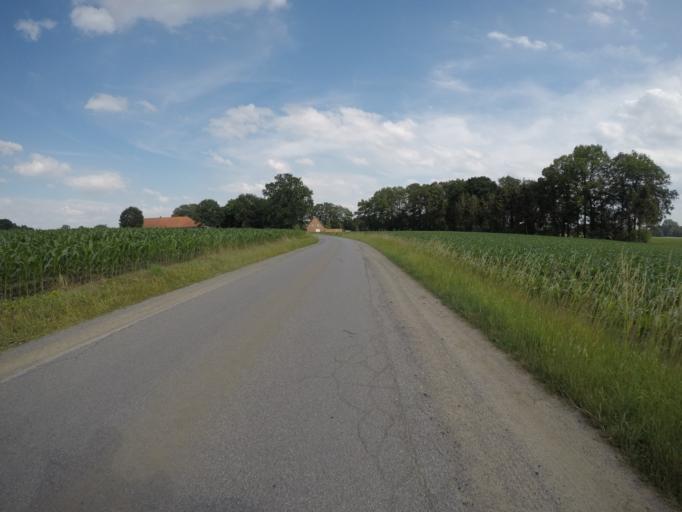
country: DE
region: North Rhine-Westphalia
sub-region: Regierungsbezirk Munster
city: Coesfeld
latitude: 51.9036
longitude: 7.1515
